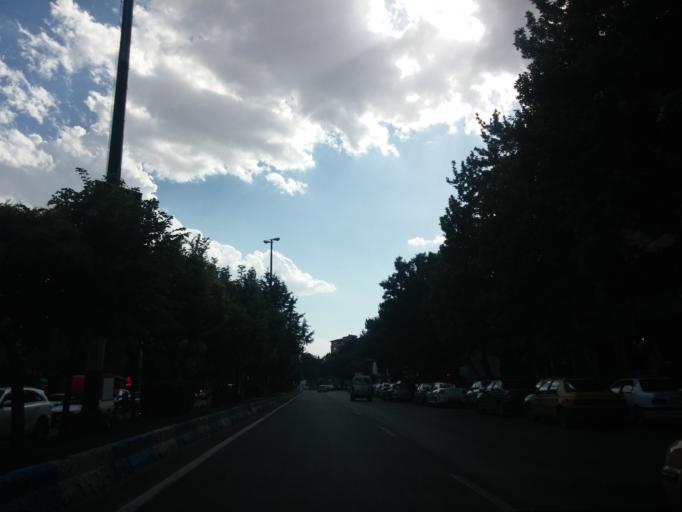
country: IR
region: Tehran
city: Damavand
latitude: 35.7362
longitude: 51.9114
